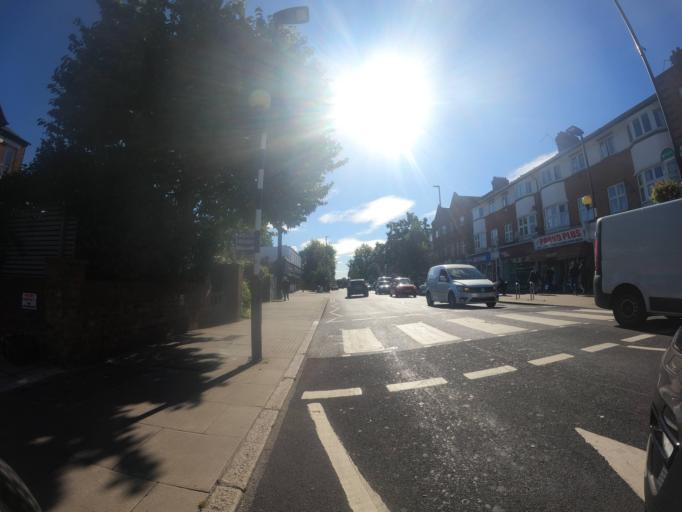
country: GB
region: England
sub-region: Greater London
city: Ealing
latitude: 51.5005
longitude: -0.3064
